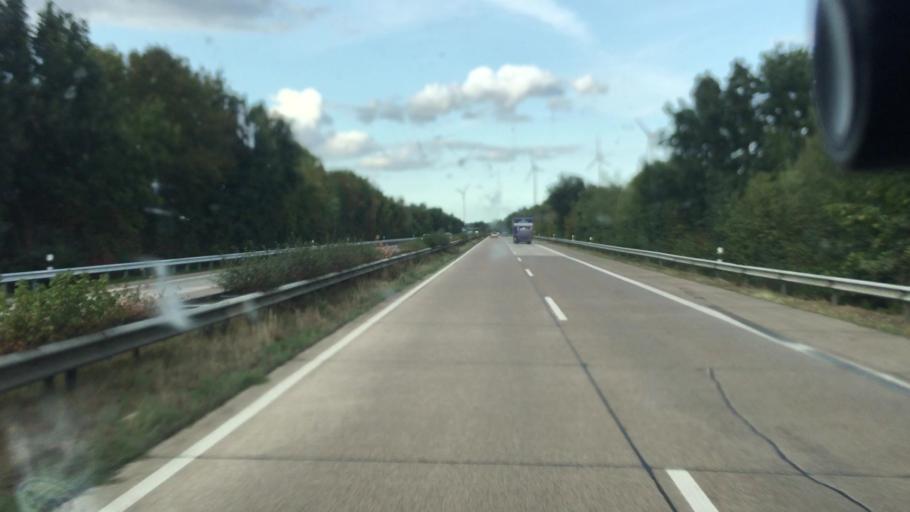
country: DE
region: Lower Saxony
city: Wardenburg
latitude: 52.9913
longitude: 8.1995
